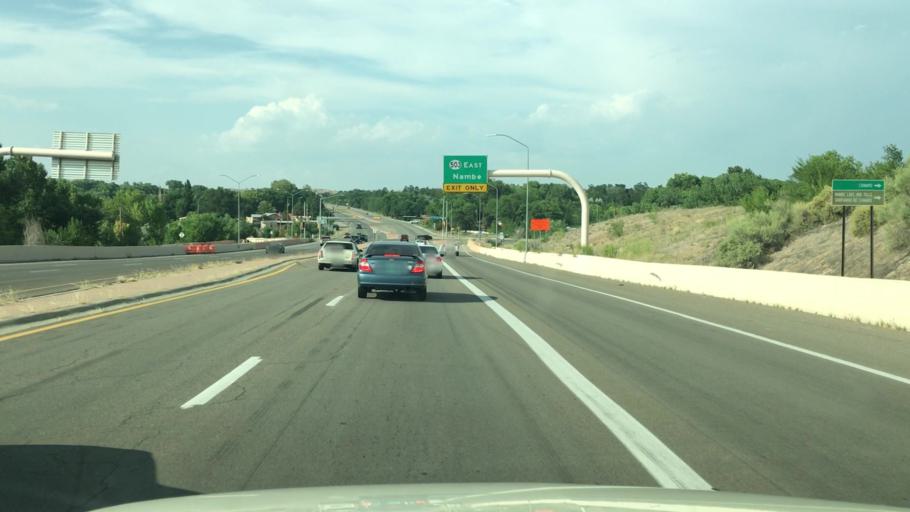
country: US
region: New Mexico
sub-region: Santa Fe County
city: Pojoaque
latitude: 35.8952
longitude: -106.0221
